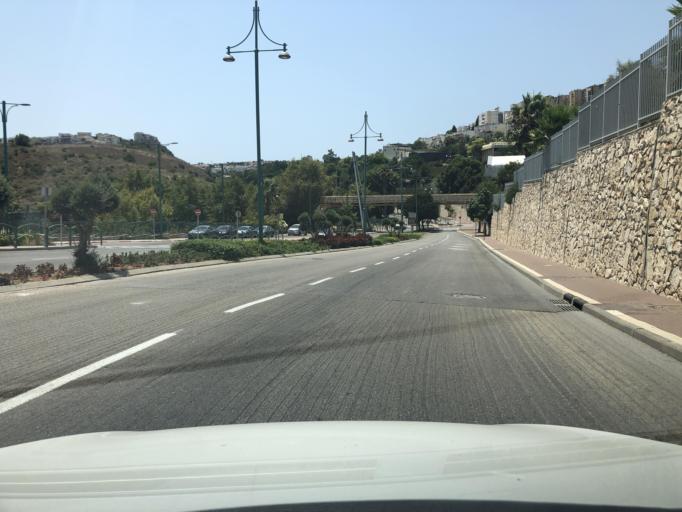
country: IL
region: Haifa
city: Daliyat el Karmil
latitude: 32.6525
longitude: 35.1068
